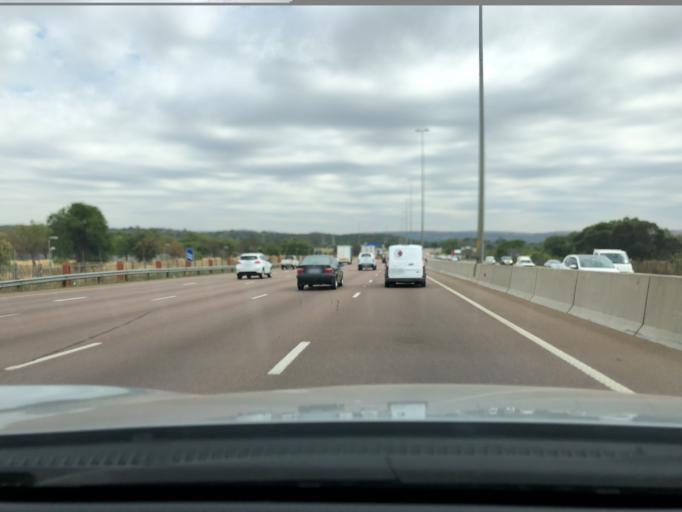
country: ZA
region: Gauteng
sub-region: City of Tshwane Metropolitan Municipality
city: Pretoria
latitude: -25.7490
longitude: 28.2715
